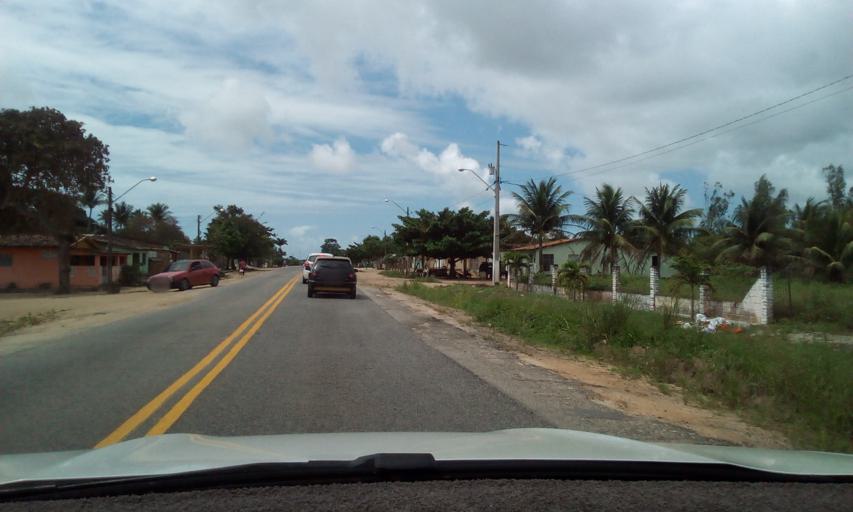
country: BR
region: Paraiba
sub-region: Rio Tinto
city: Rio Tinto
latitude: -6.7700
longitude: -35.0199
